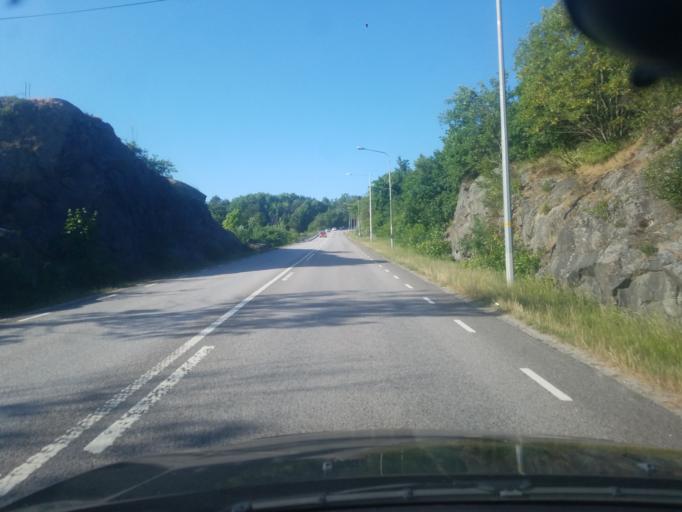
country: SE
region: Vaestra Goetaland
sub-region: Orust
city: Henan
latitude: 58.2408
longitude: 11.6804
